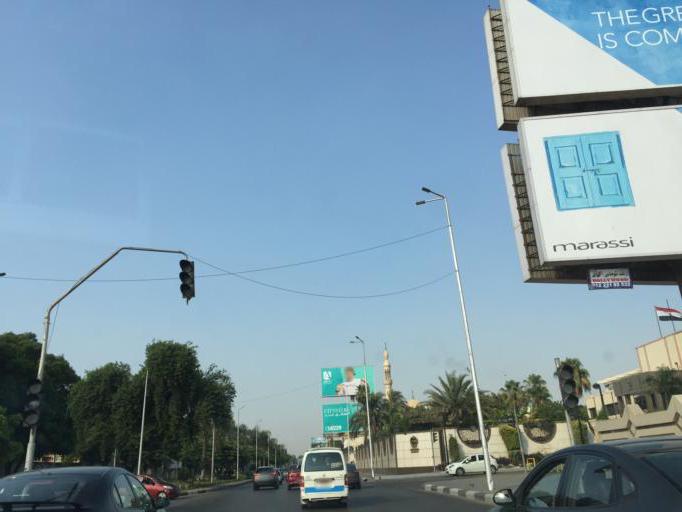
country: EG
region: Muhafazat al Qahirah
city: Cairo
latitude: 30.0824
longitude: 31.3193
